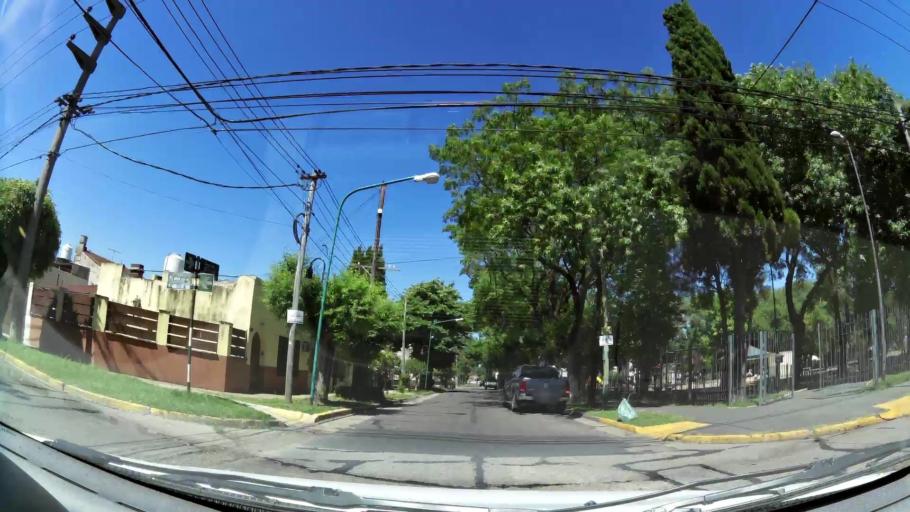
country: AR
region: Buenos Aires
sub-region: Partido de General San Martin
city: General San Martin
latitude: -34.5303
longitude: -58.5499
